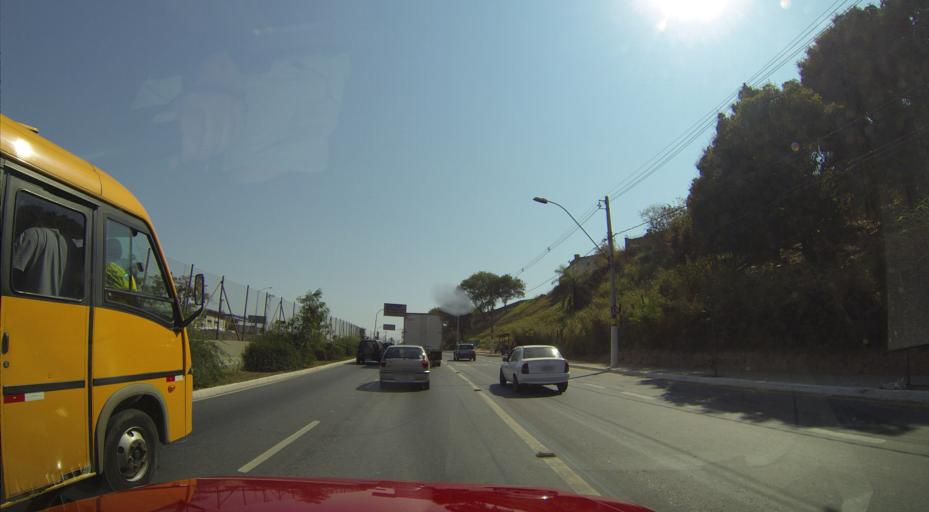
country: BR
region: Minas Gerais
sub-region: Belo Horizonte
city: Belo Horizonte
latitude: -19.8487
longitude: -43.9327
